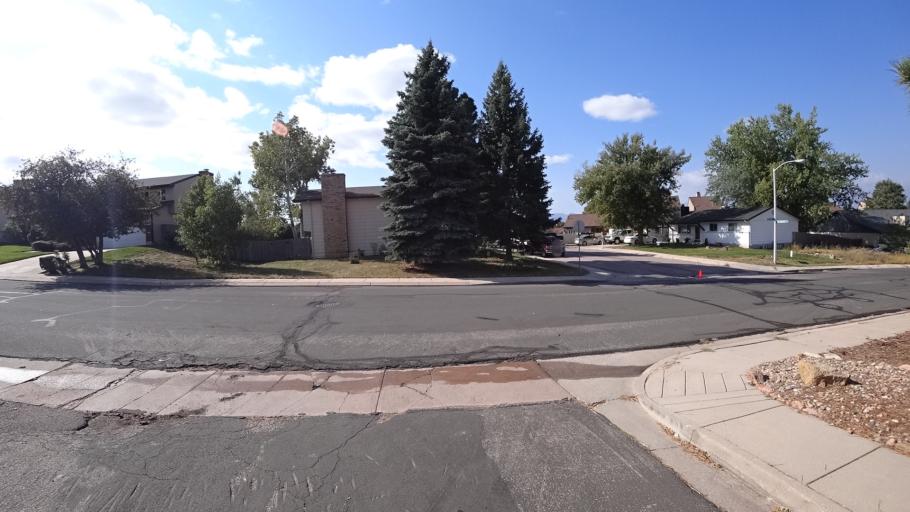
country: US
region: Colorado
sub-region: El Paso County
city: Cimarron Hills
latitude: 38.8869
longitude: -104.7344
